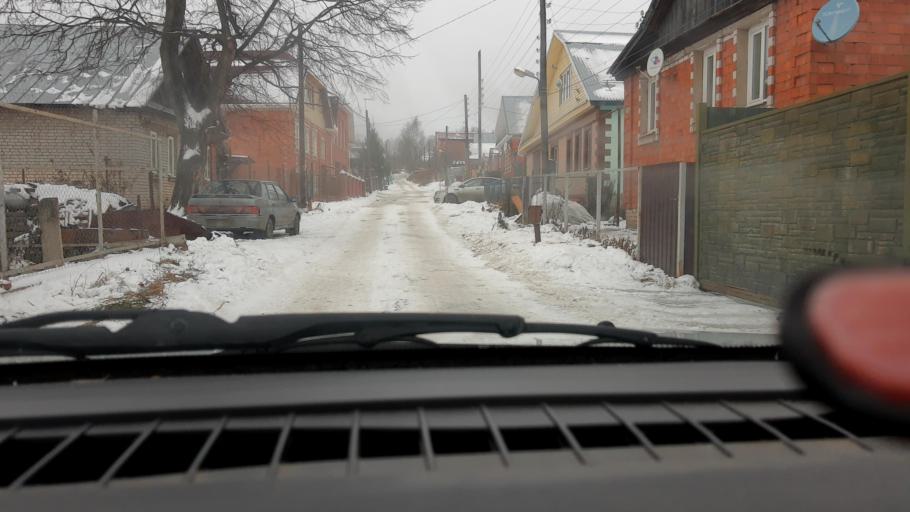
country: RU
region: Nizjnij Novgorod
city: Nizhniy Novgorod
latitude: 56.2325
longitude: 43.9847
